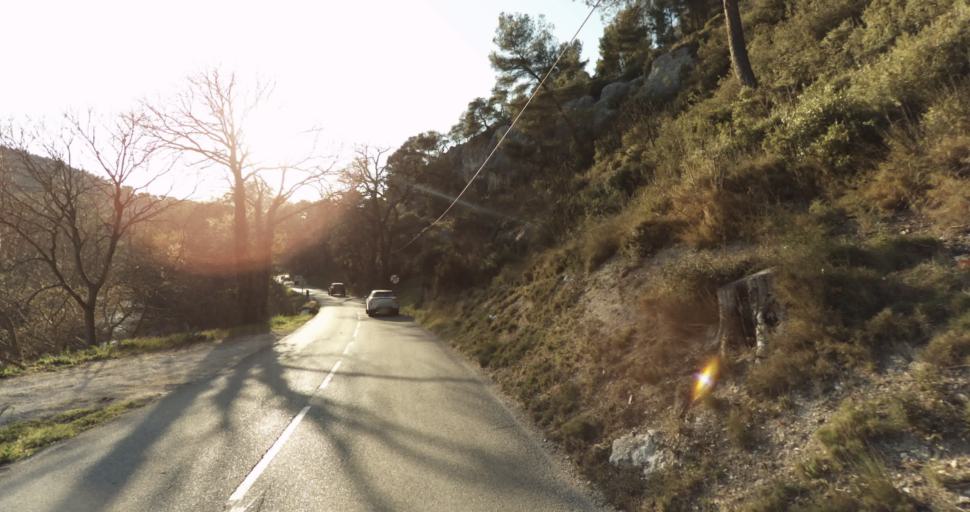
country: FR
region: Provence-Alpes-Cote d'Azur
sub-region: Departement des Bouches-du-Rhone
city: Ventabren
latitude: 43.5190
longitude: 5.3012
